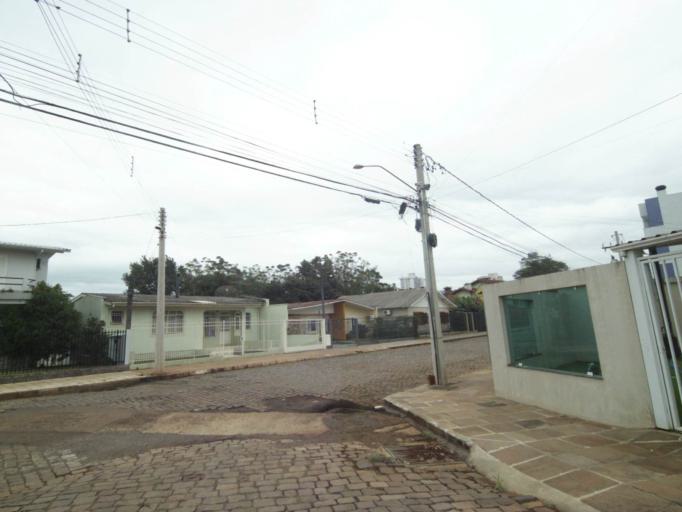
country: BR
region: Rio Grande do Sul
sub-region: Lagoa Vermelha
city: Lagoa Vermelha
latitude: -28.2150
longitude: -51.5210
